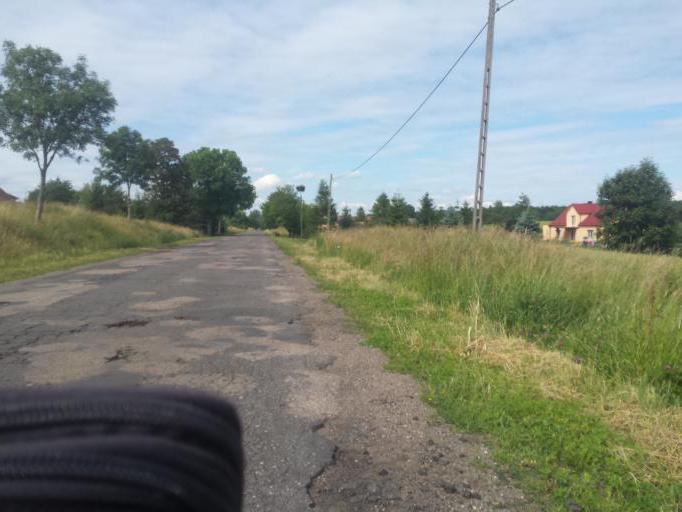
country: PL
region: Warmian-Masurian Voivodeship
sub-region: Powiat ilawski
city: Ilawa
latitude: 53.6091
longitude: 19.4440
